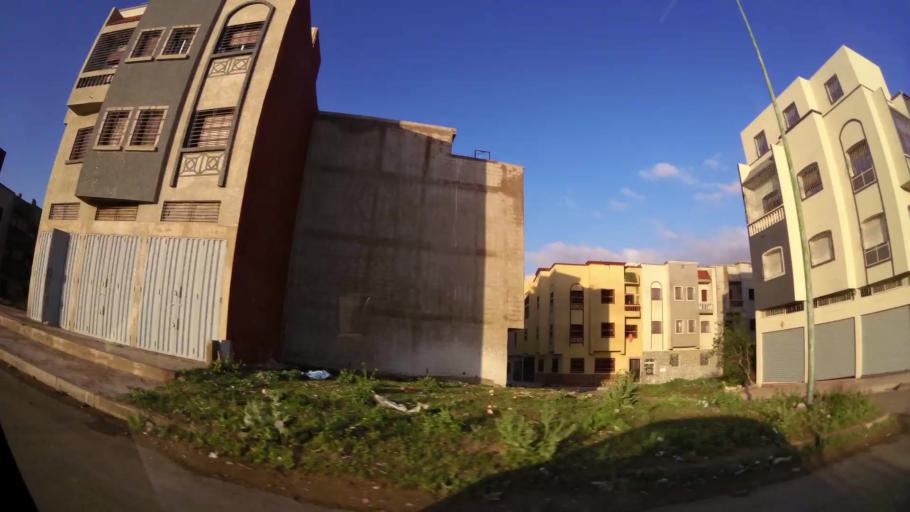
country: MA
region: Chaouia-Ouardigha
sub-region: Settat Province
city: Settat
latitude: 32.9843
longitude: -7.5990
